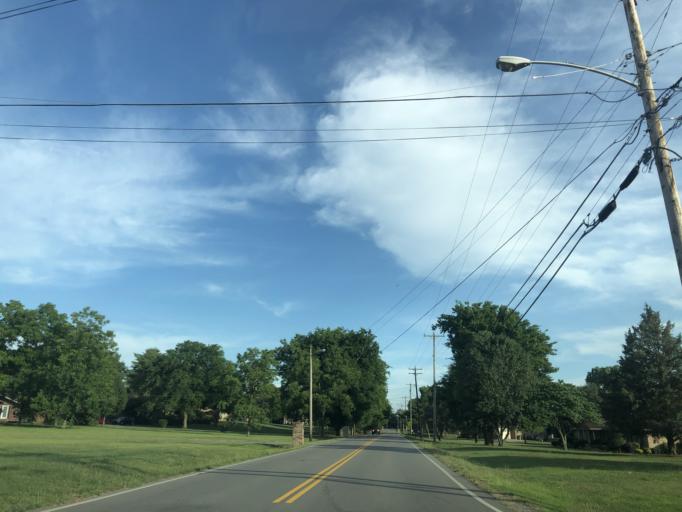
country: US
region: Tennessee
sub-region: Davidson County
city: Nashville
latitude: 36.2128
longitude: -86.8639
